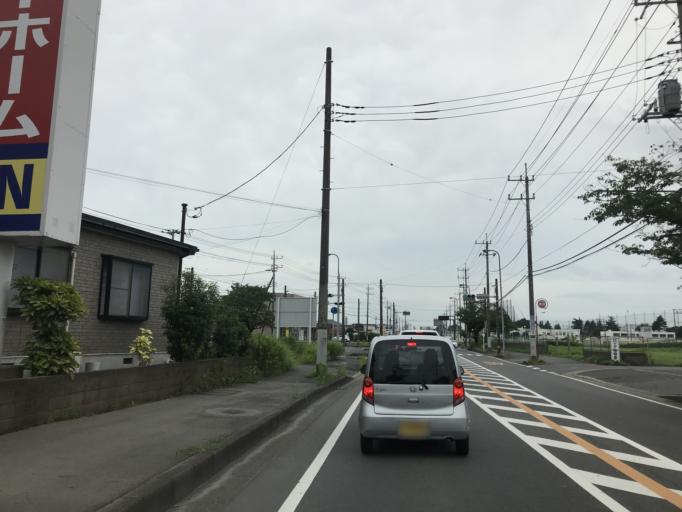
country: JP
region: Ibaraki
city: Mito-shi
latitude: 36.3262
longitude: 140.4577
